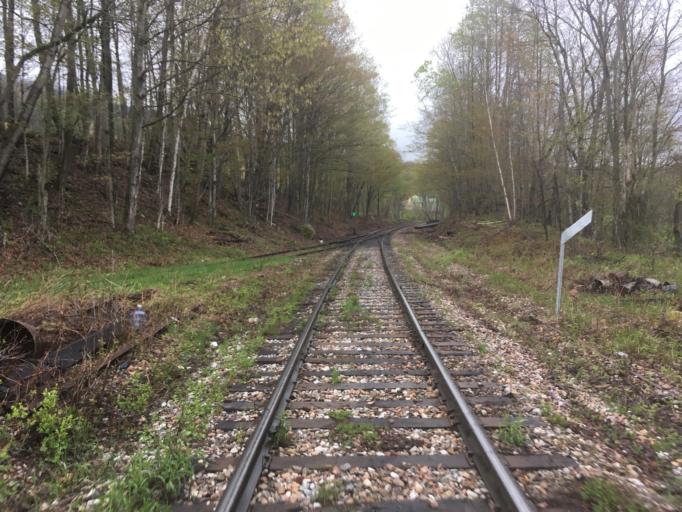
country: US
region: Vermont
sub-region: Rutland County
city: Rutland
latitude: 43.4919
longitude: -72.8808
